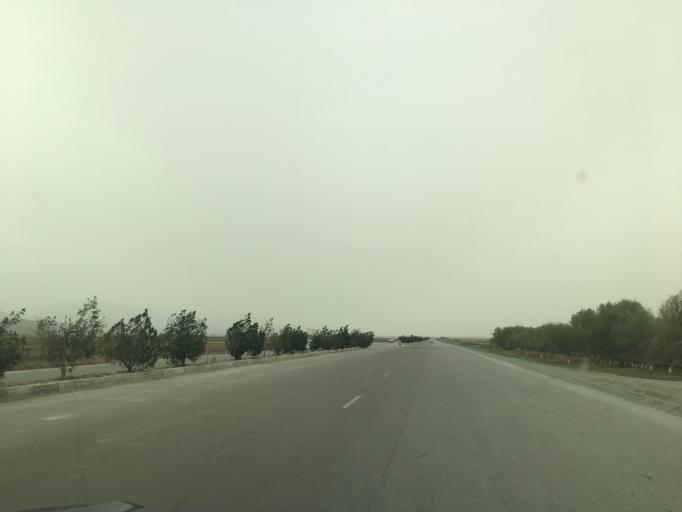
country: TM
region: Ahal
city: Baharly
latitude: 38.3474
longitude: 57.5538
